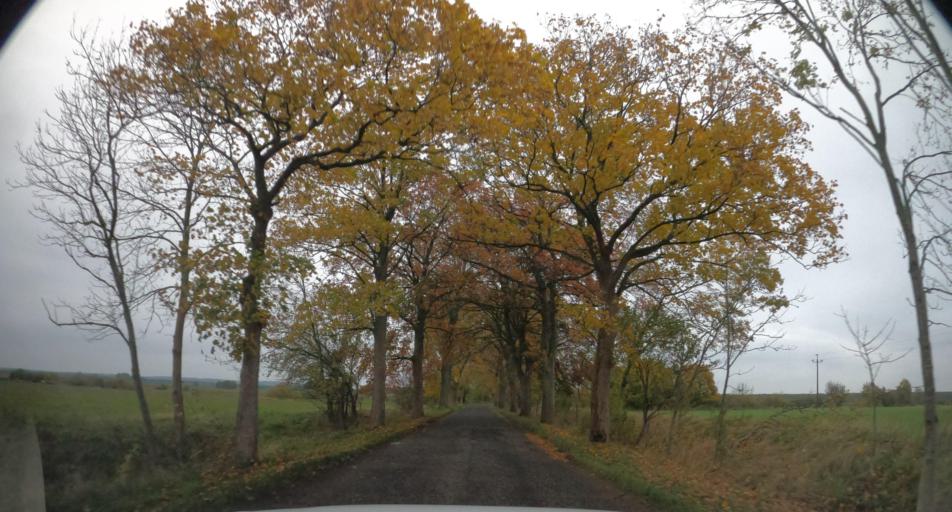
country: PL
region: West Pomeranian Voivodeship
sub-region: Powiat kamienski
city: Wolin
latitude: 53.9235
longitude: 14.6100
